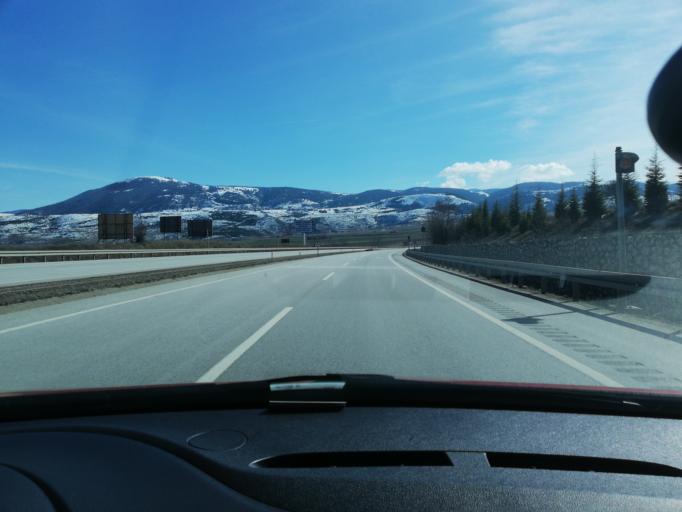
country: TR
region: Karabuk
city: Gozyeri
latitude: 40.8808
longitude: 32.5792
